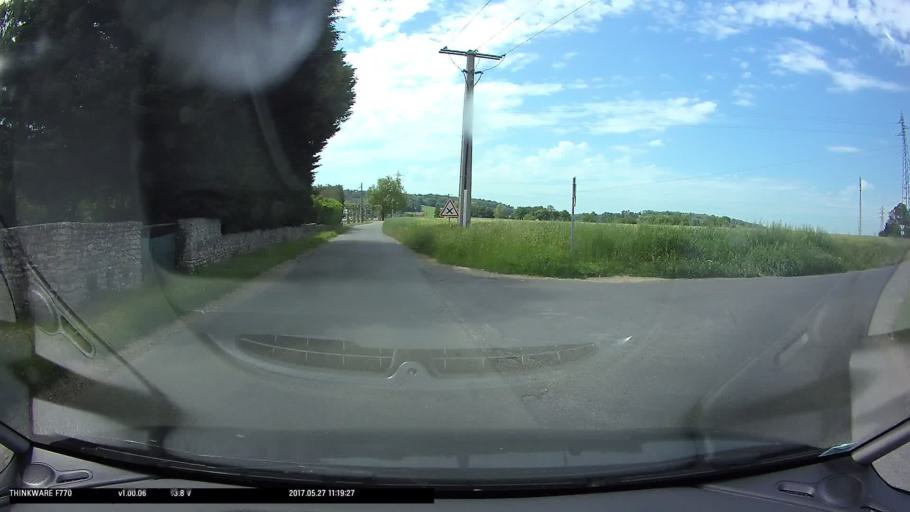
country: FR
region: Picardie
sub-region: Departement de l'Oise
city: Trie-Chateau
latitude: 49.2892
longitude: 1.8298
